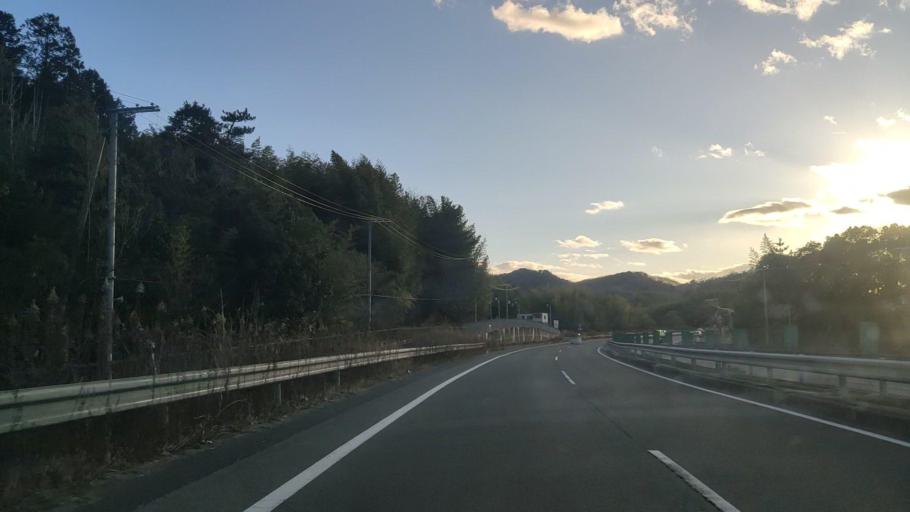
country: JP
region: Hyogo
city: Tatsunocho-tominaga
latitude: 34.8622
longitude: 134.6180
